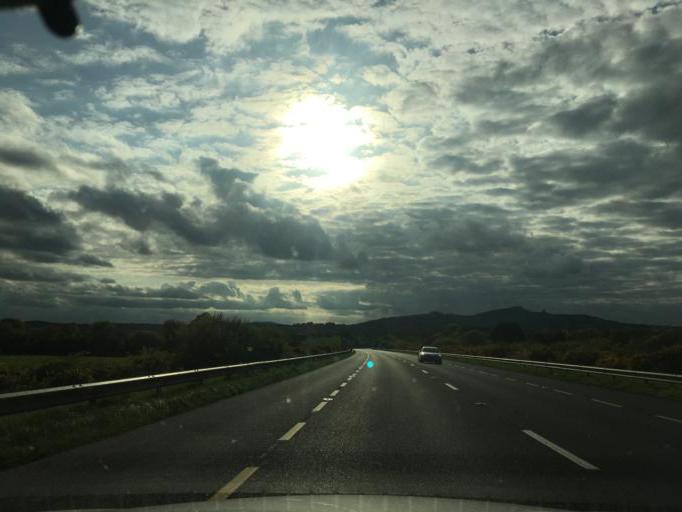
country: IE
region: Leinster
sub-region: Loch Garman
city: New Ross
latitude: 52.3617
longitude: -6.7248
